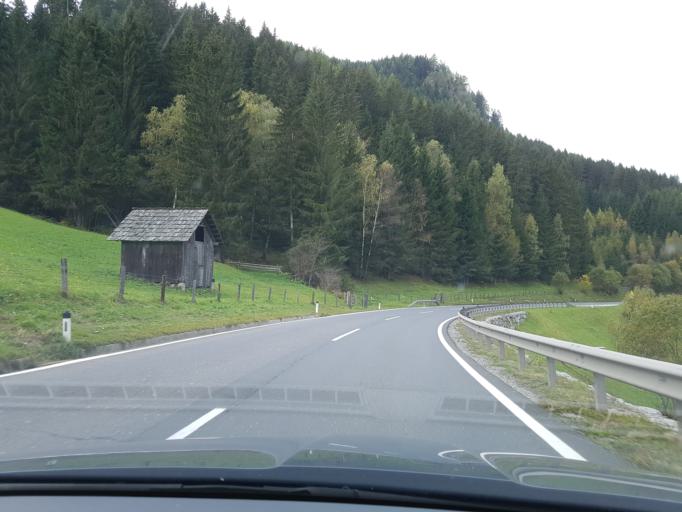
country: AT
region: Salzburg
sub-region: Politischer Bezirk Tamsweg
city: Ramingstein
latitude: 47.0708
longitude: 13.8688
